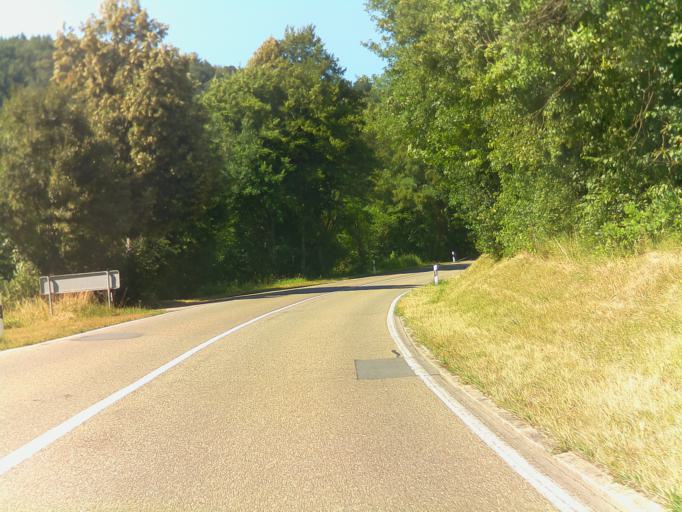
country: DE
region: Baden-Wuerttemberg
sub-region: Regierungsbezirk Stuttgart
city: Wertheim
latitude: 49.7458
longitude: 9.5113
